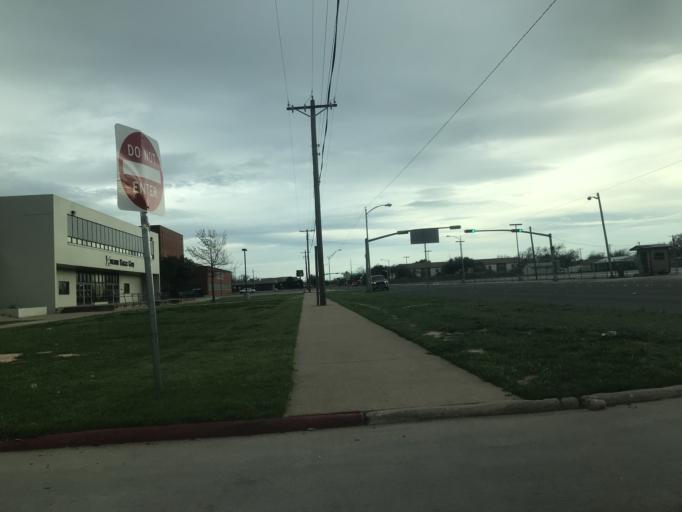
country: US
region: Texas
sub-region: Taylor County
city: Abilene
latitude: 32.4573
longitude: -99.7576
